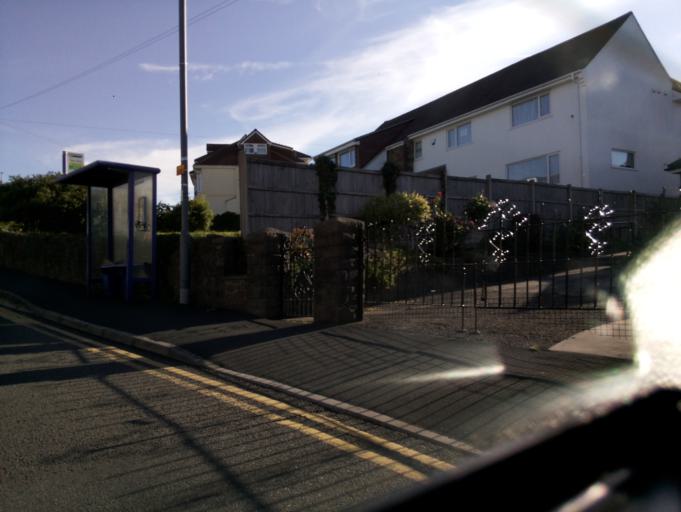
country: GB
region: England
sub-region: South Gloucestershire
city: Kingswood
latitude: 51.4674
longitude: -2.5110
